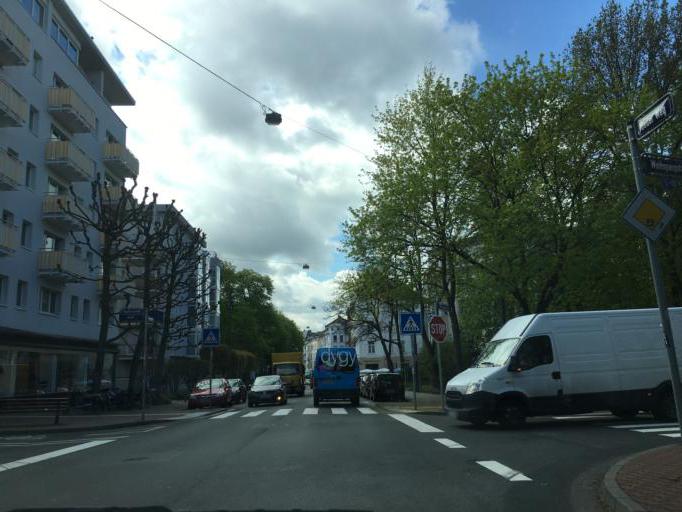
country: DE
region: Hesse
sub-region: Regierungsbezirk Darmstadt
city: Frankfurt am Main
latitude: 50.1254
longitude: 8.6820
